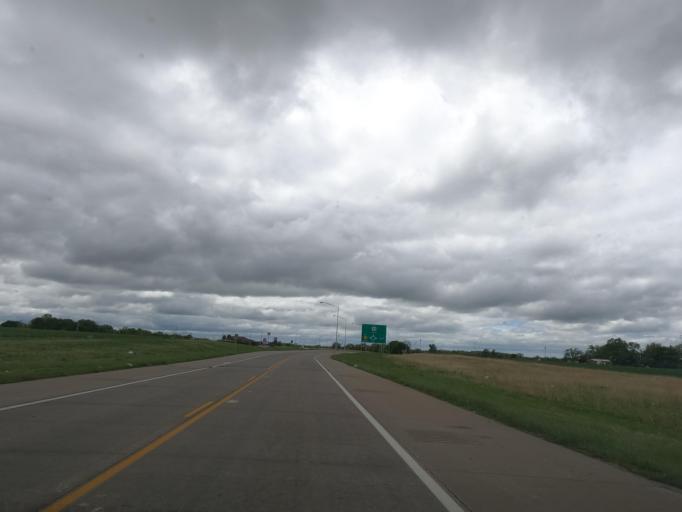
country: US
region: Kansas
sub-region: Wilson County
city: Fredonia
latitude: 37.5331
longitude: -95.8013
